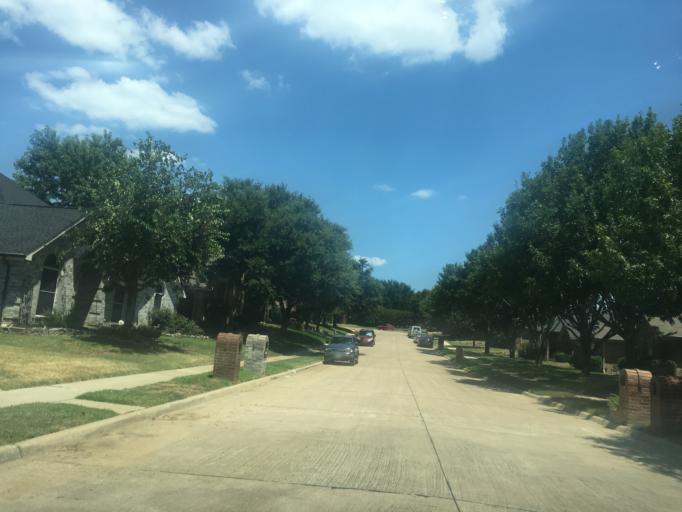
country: US
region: Texas
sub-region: Denton County
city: Lewisville
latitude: 33.0223
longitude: -97.0007
